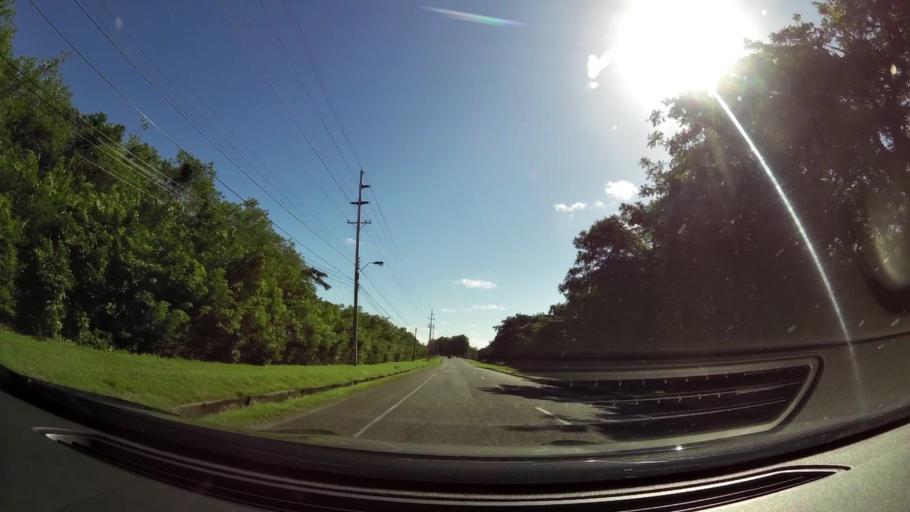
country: TT
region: Tobago
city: Scarborough
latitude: 11.1549
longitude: -60.7913
